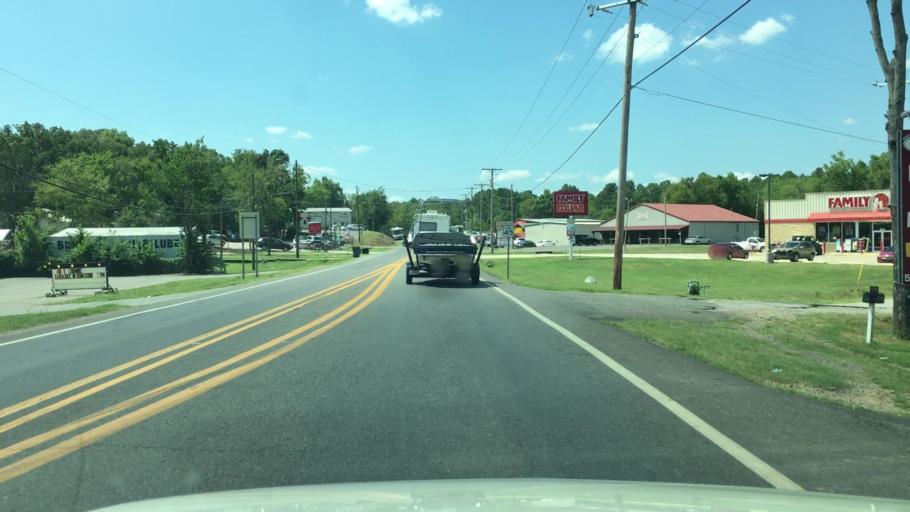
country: US
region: Arkansas
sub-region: Garland County
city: Piney
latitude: 34.5057
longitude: -93.1288
